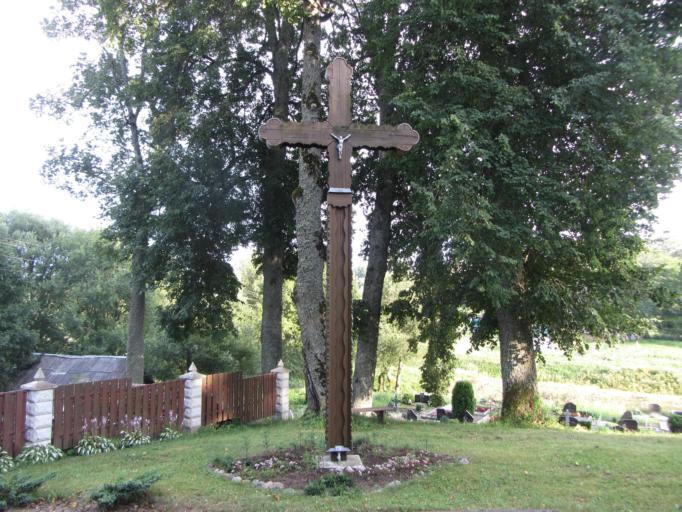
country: LT
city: Moletai
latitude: 55.1175
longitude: 25.3966
